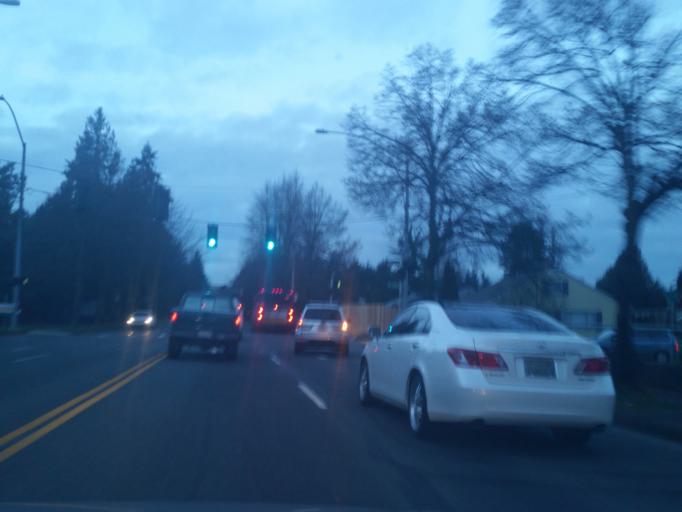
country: US
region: Washington
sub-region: King County
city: Shoreline
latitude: 47.7263
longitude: -122.3127
